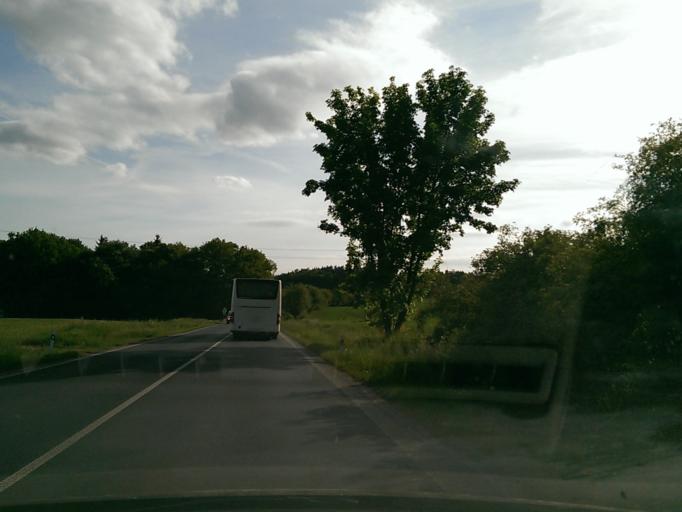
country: CZ
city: Duba
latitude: 50.5346
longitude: 14.5247
